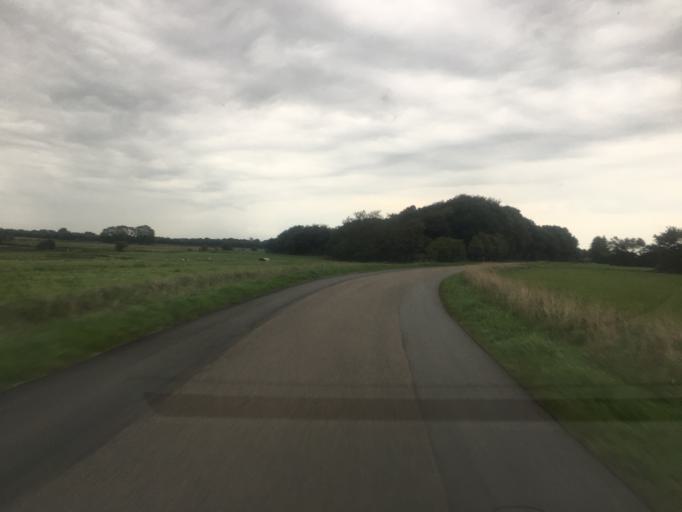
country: DK
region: South Denmark
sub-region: Tonder Kommune
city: Logumkloster
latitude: 54.9996
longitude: 9.0223
